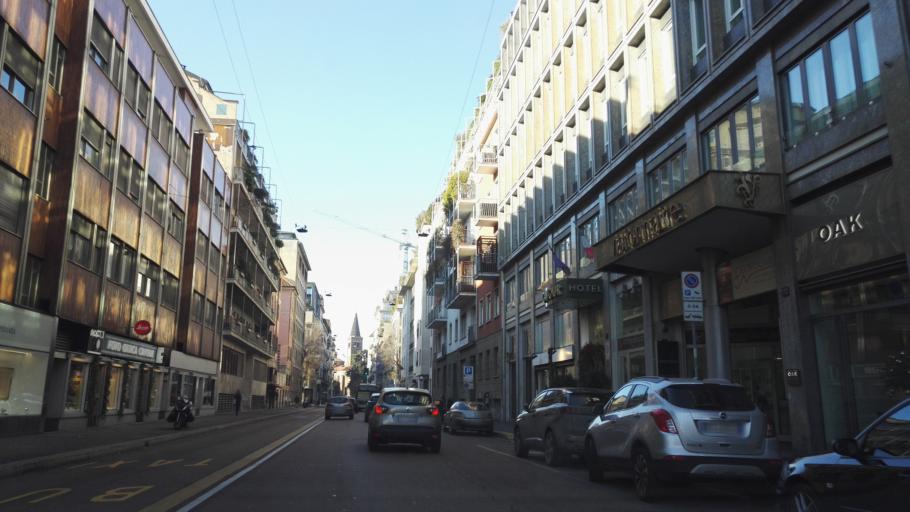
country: IT
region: Lombardy
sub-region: Citta metropolitana di Milano
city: Milano
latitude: 45.4725
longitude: 9.1947
